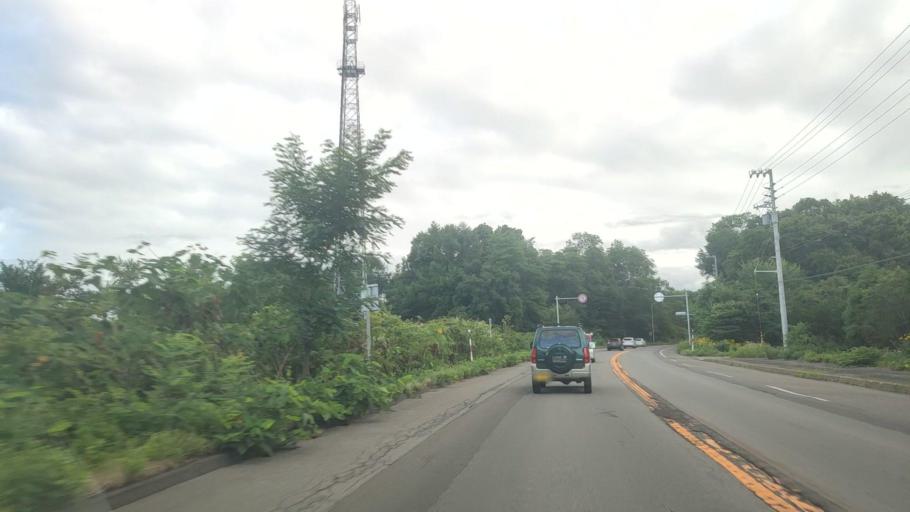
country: JP
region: Hokkaido
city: Nanae
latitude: 42.0667
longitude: 140.6032
